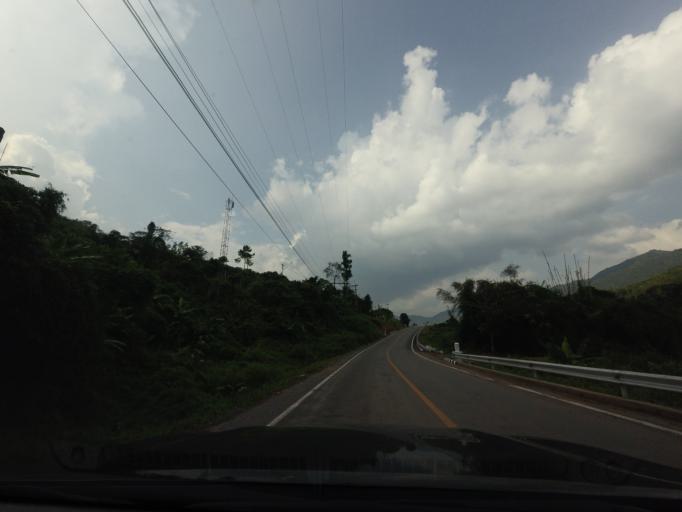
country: TH
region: Nan
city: Bo Kluea
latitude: 19.2075
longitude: 101.1856
